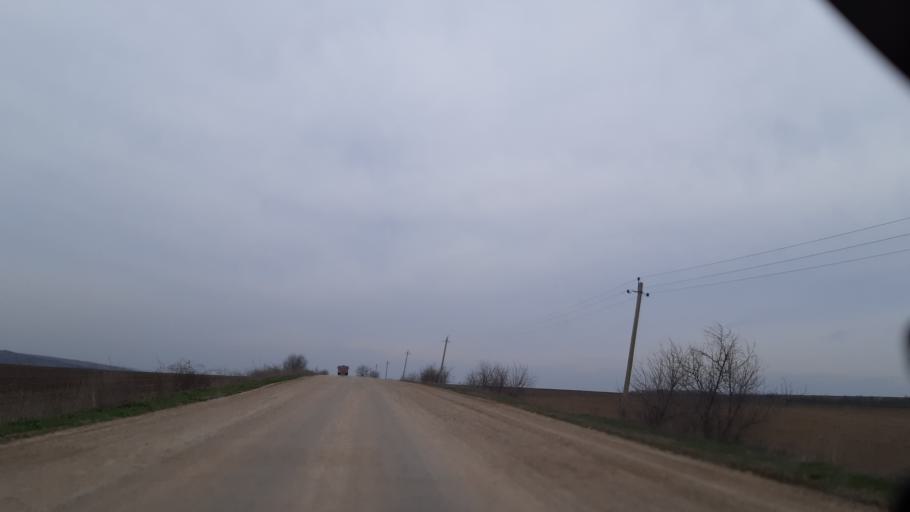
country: MD
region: Orhei
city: Orhei
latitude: 47.5901
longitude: 28.6476
